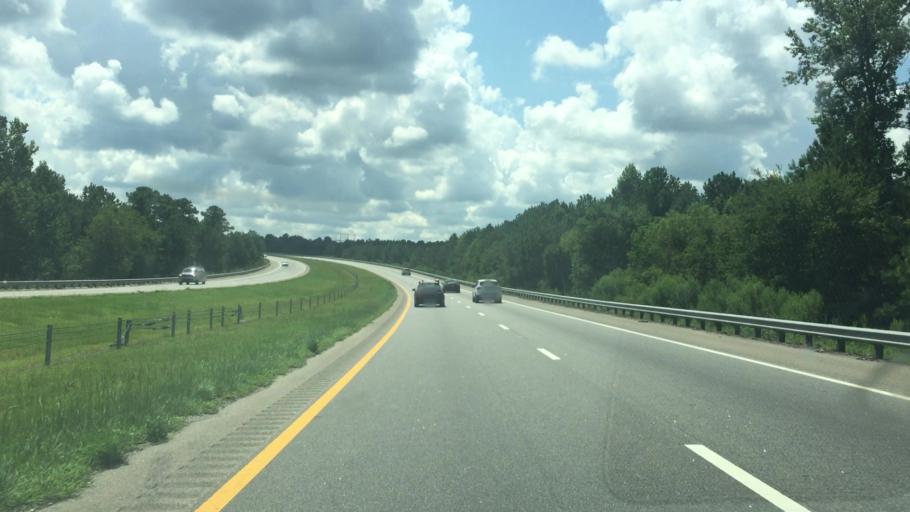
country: US
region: North Carolina
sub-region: Richmond County
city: East Rockingham
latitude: 34.8883
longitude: -79.7889
